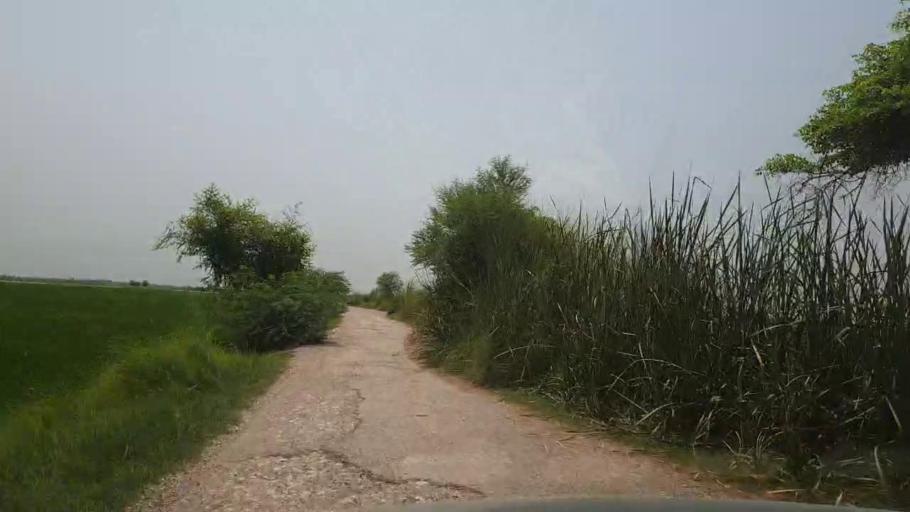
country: PK
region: Sindh
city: Garhi Yasin
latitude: 27.8728
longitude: 68.5009
